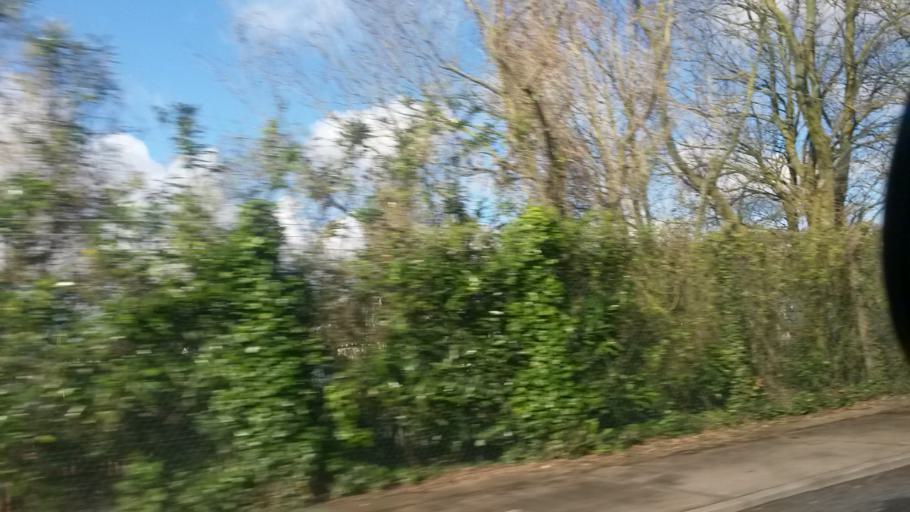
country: IE
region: Munster
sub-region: County Cork
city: Cobh
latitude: 51.8506
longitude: -8.3246
